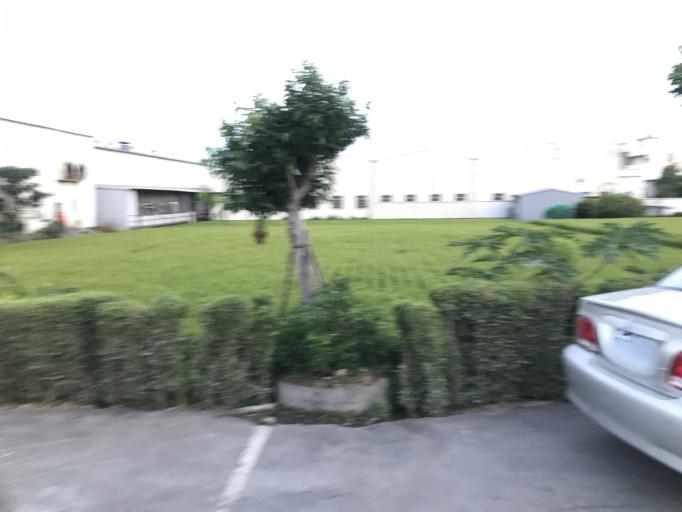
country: TW
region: Taiwan
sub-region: Taichung City
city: Taichung
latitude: 24.1218
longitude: 120.6348
